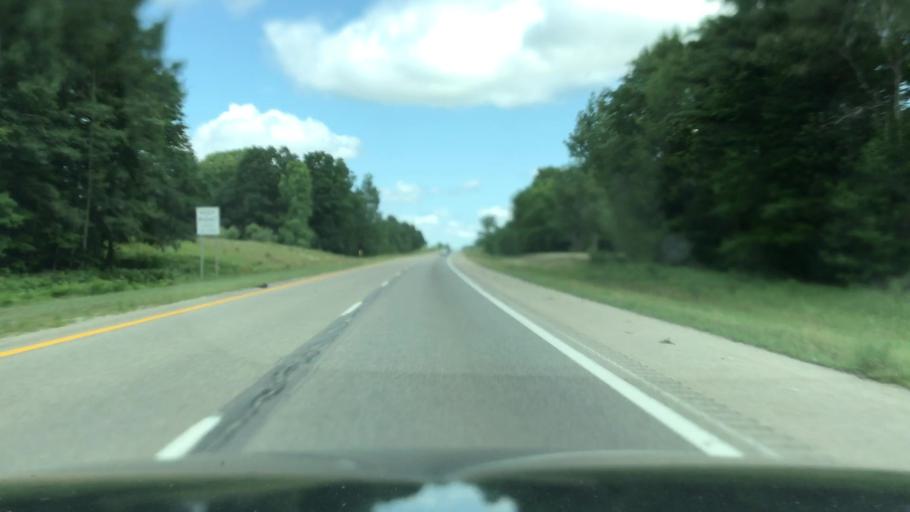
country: US
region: Michigan
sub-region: Mecosta County
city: Big Rapids
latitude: 43.7021
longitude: -85.5277
